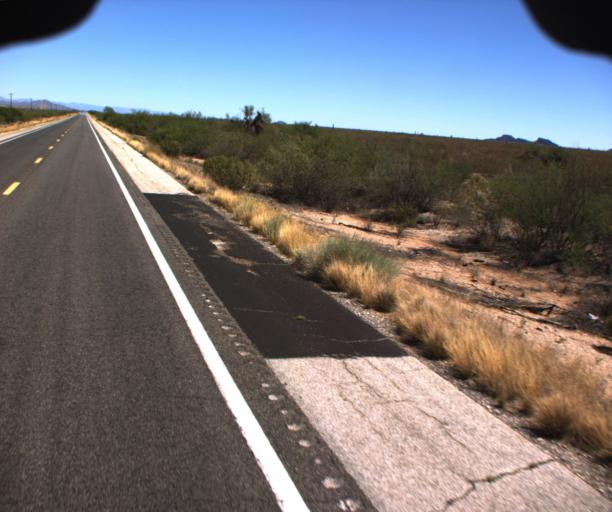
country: US
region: Arizona
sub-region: La Paz County
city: Salome
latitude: 33.9138
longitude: -113.2671
